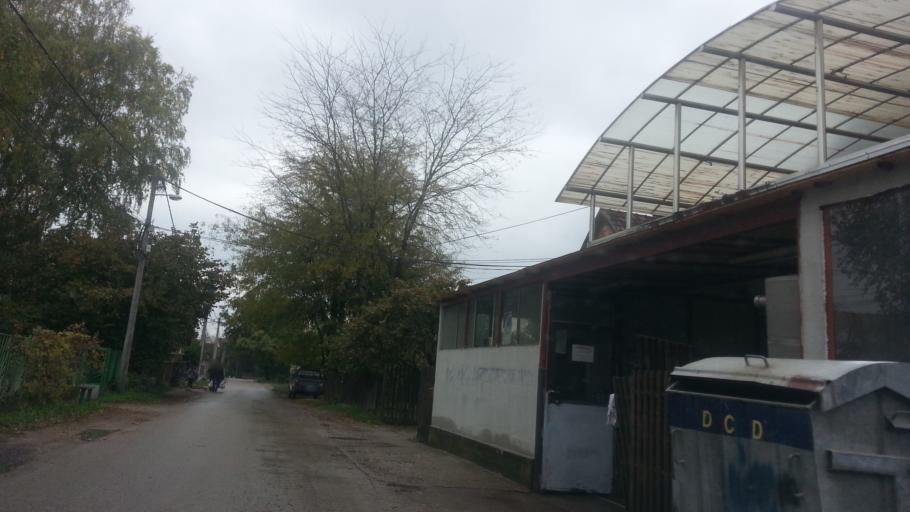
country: RS
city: Novi Banovci
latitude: 44.9129
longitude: 20.2848
